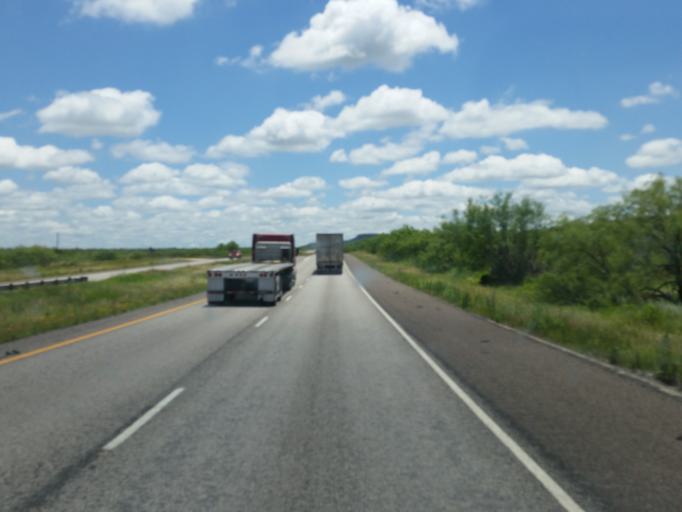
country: US
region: Texas
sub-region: Scurry County
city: Snyder
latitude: 32.9829
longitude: -101.1188
